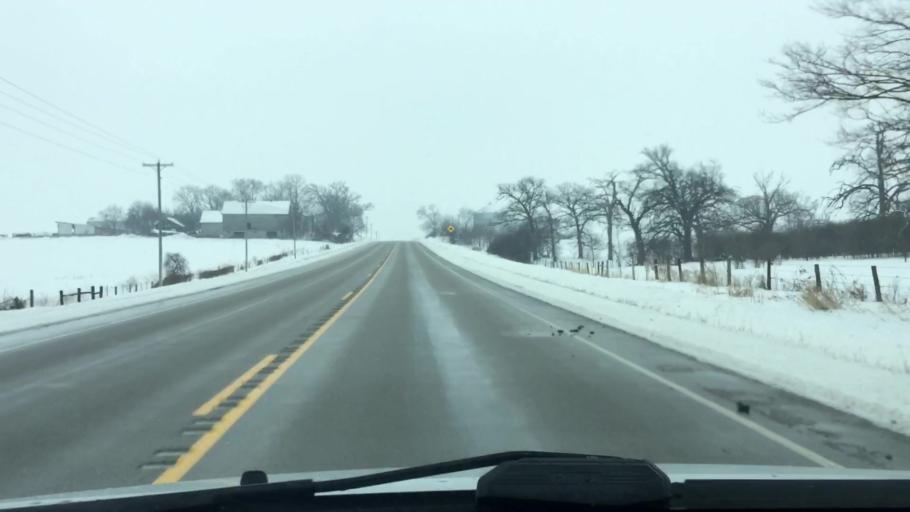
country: US
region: Illinois
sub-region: McHenry County
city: Hebron
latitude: 42.5304
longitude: -88.4429
